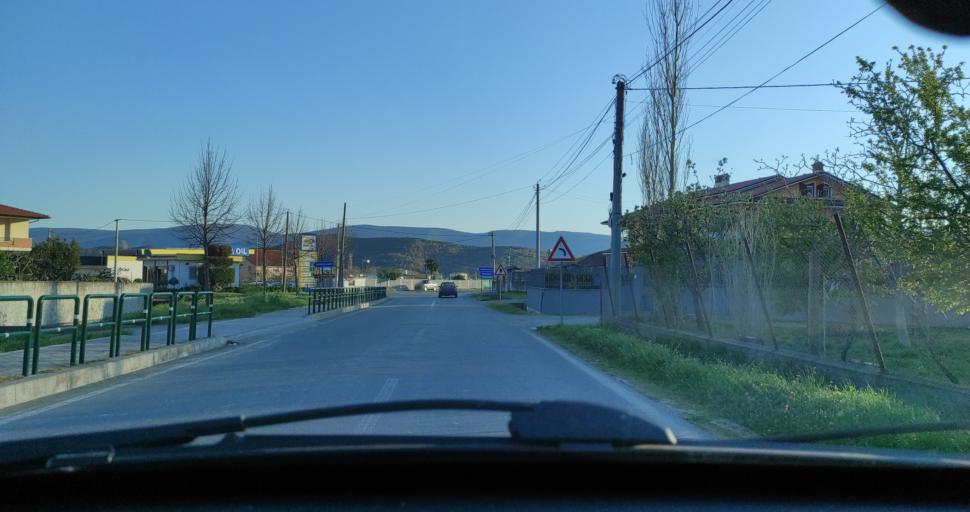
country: AL
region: Shkoder
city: Vukatane
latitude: 41.9531
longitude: 19.5288
